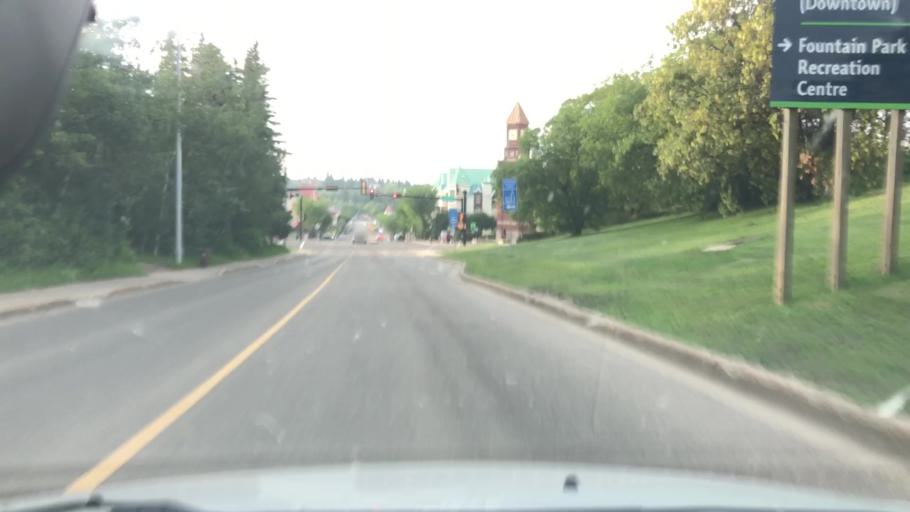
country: CA
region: Alberta
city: St. Albert
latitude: 53.6311
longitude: -113.6226
